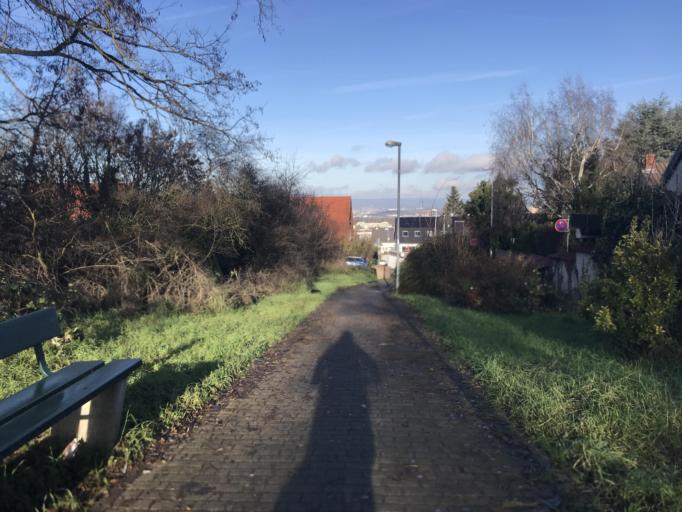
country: DE
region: Rheinland-Pfalz
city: Mainz
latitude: 49.9696
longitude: 8.2863
